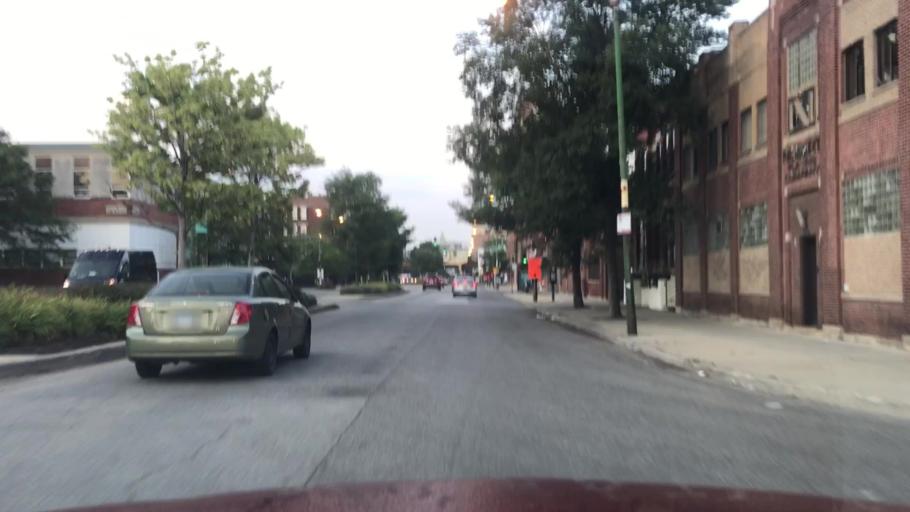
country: US
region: Illinois
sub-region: Cook County
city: Chicago
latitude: 41.8878
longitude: -87.6672
